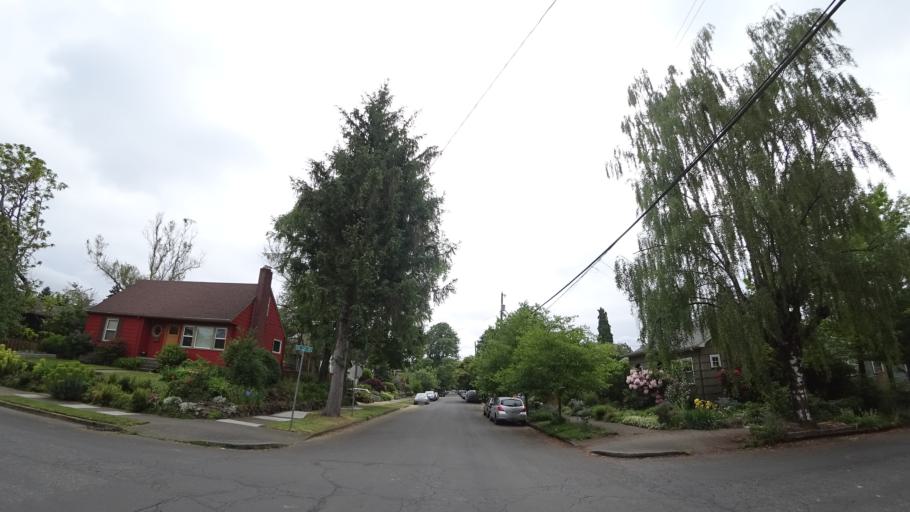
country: US
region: Oregon
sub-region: Multnomah County
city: Portland
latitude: 45.5005
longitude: -122.6316
